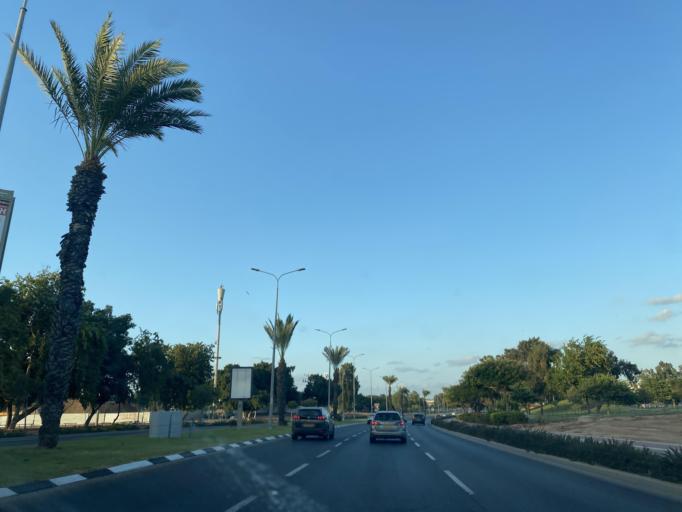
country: IL
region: Southern District
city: Ashdod
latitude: 31.8009
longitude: 34.6559
